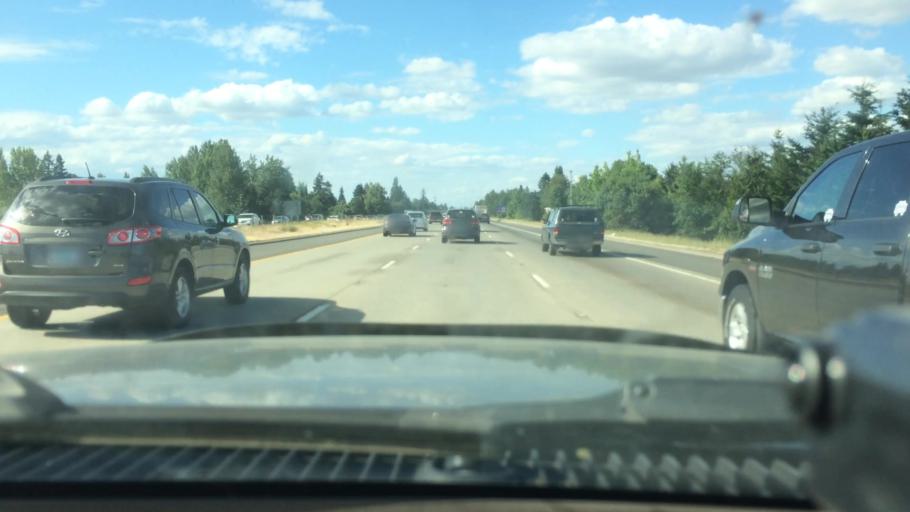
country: US
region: Oregon
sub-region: Marion County
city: Four Corners
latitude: 44.9314
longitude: -122.9902
